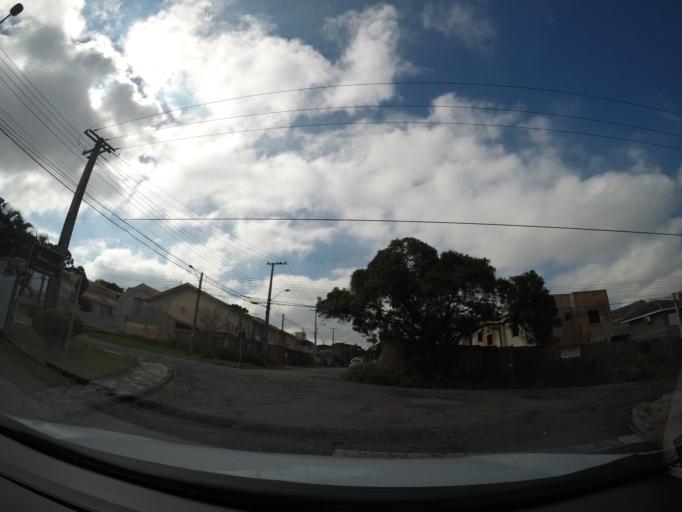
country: BR
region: Parana
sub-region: Sao Jose Dos Pinhais
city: Sao Jose dos Pinhais
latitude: -25.4936
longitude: -49.2175
